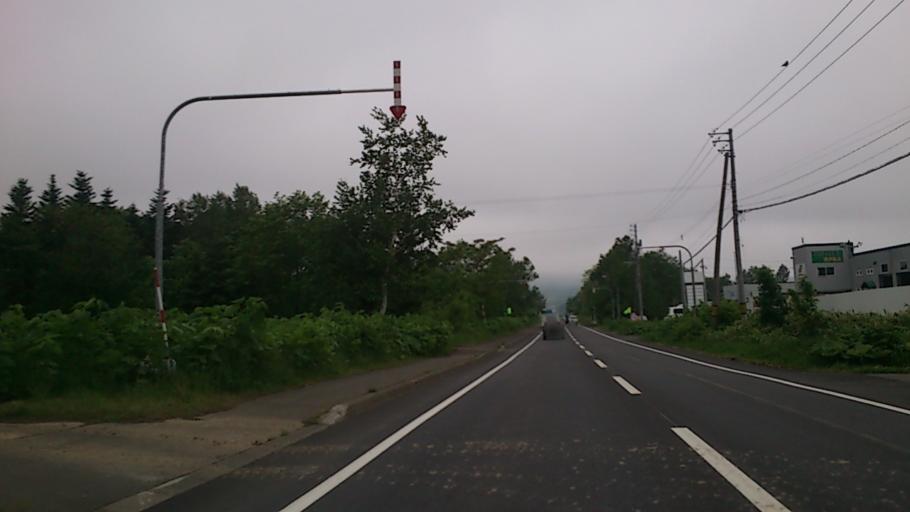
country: JP
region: Hokkaido
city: Niseko Town
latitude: 42.8835
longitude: 140.7623
